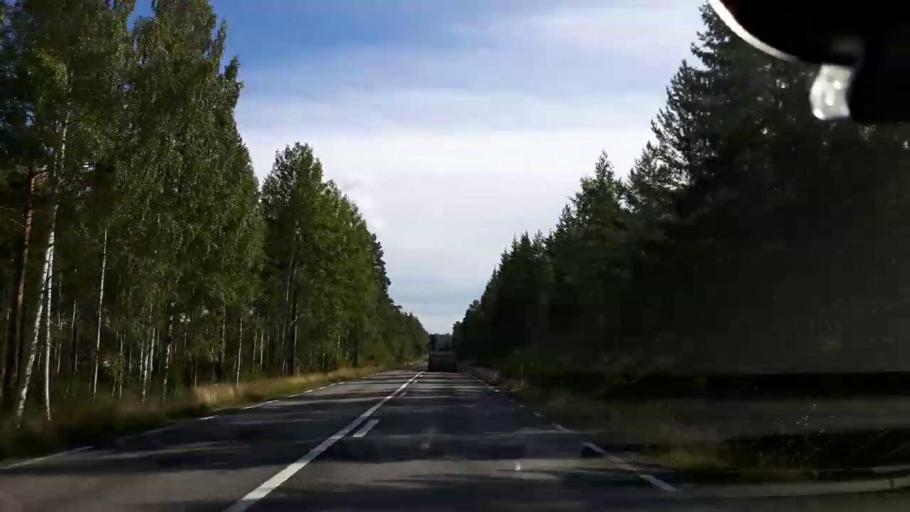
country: SE
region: Jaemtland
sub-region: Braecke Kommun
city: Braecke
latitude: 63.1890
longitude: 15.4758
